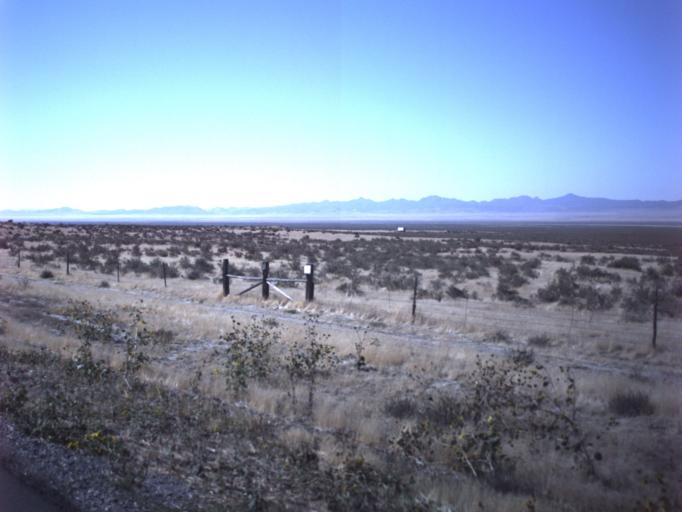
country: US
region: Utah
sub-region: Tooele County
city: Grantsville
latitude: 40.5118
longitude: -112.7477
